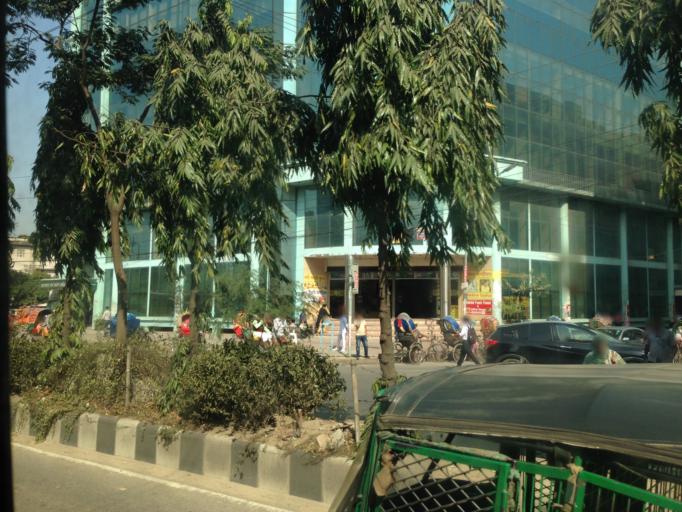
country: BD
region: Dhaka
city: Azimpur
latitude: 23.7452
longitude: 90.3819
